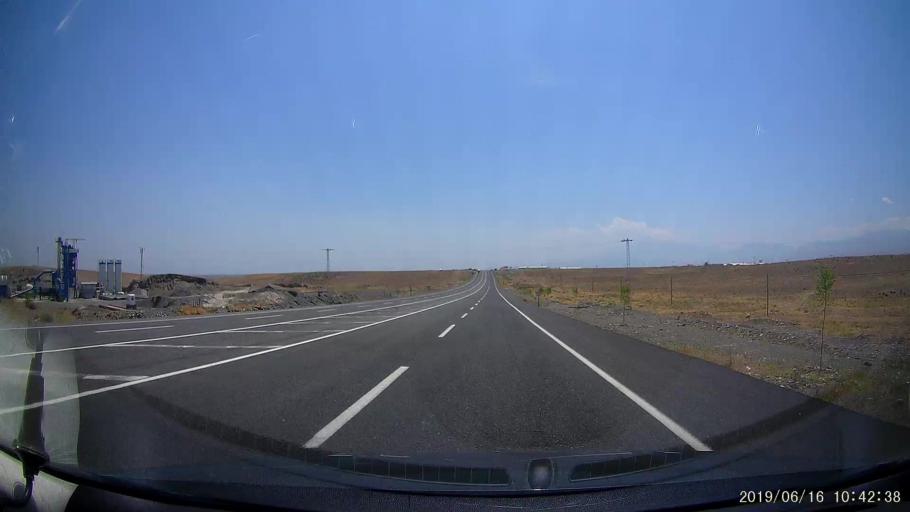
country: AM
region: Armavir
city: Shenavan
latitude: 40.0407
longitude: 43.8109
